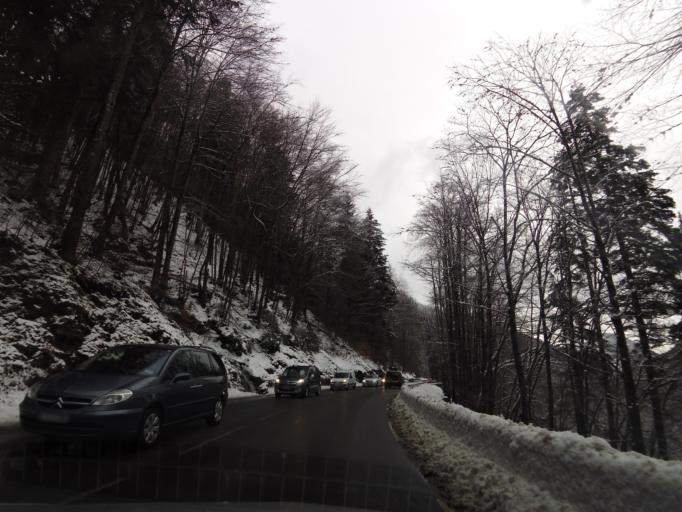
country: FR
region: Rhone-Alpes
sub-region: Departement de la Haute-Savoie
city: Taninges
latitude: 46.1245
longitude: 6.6222
